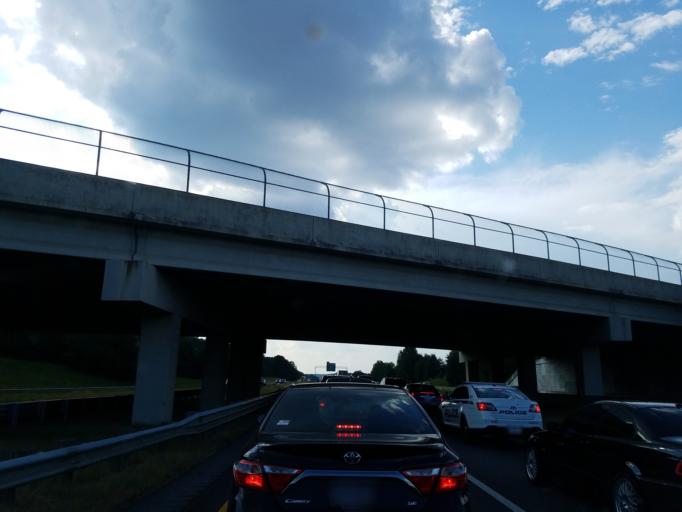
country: US
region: Georgia
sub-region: Gwinnett County
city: Lawrenceville
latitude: 33.9606
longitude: -84.0603
